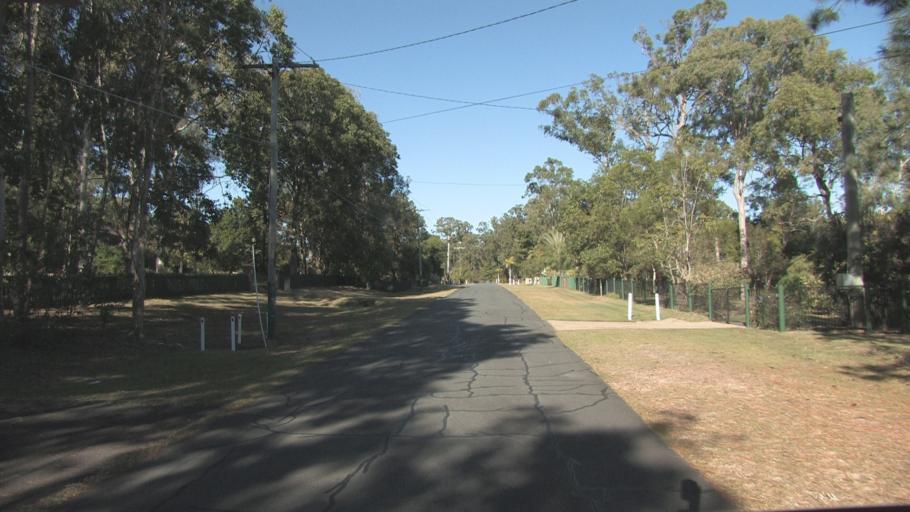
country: AU
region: Queensland
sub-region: Brisbane
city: Forest Lake
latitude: -27.6636
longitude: 153.0113
